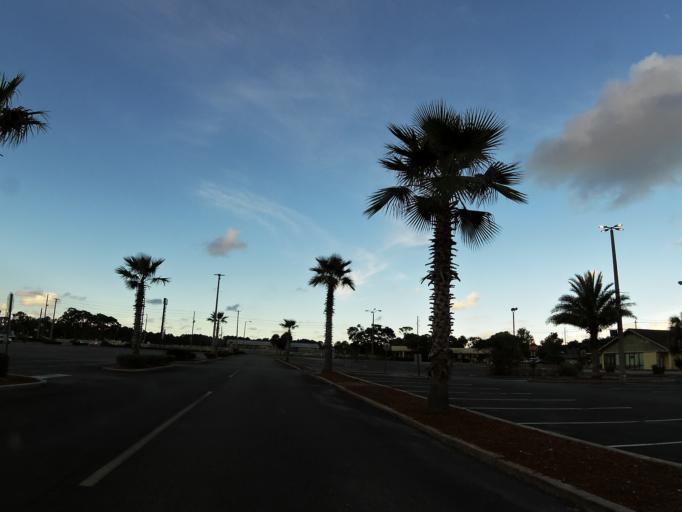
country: US
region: Georgia
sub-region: Camden County
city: St Marys
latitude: 30.7501
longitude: -81.5768
